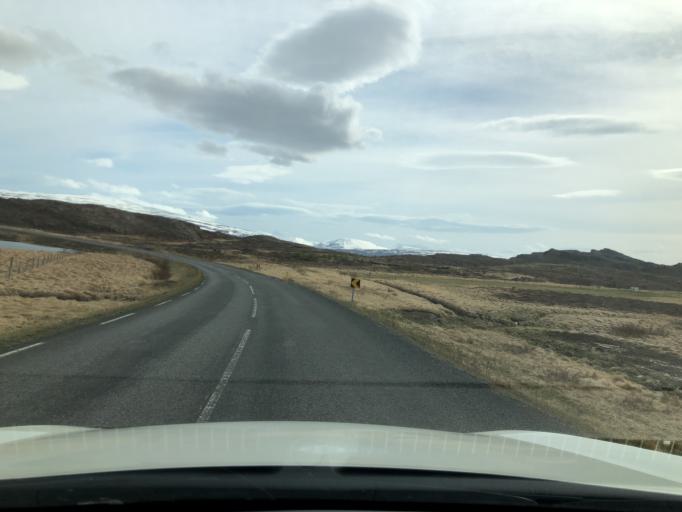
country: IS
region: East
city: Egilsstadir
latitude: 65.3014
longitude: -14.4605
